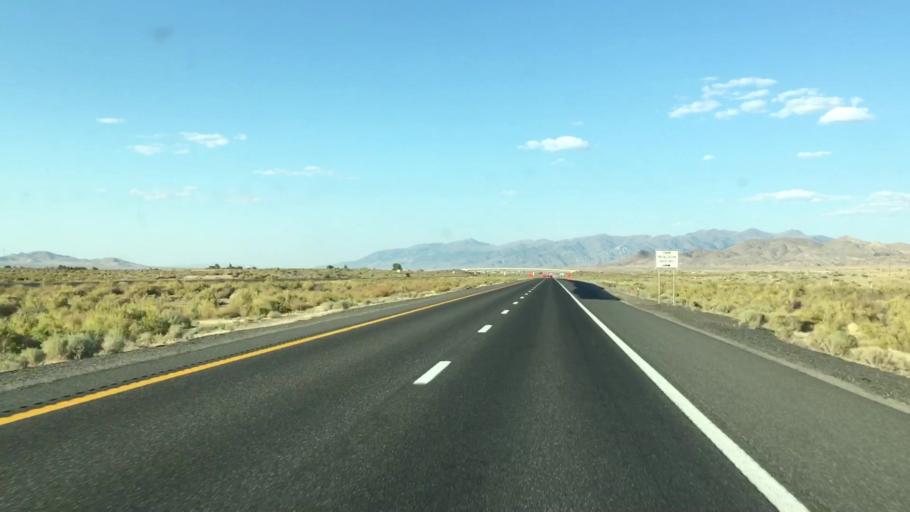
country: US
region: Nevada
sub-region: Pershing County
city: Lovelock
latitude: 40.2057
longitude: -118.4238
